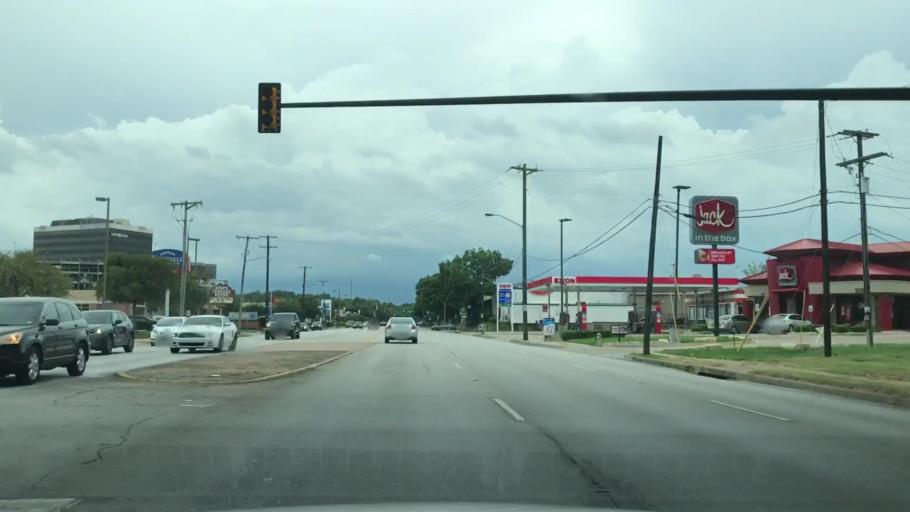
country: US
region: Texas
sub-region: Tarrant County
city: Fort Worth
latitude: 32.7309
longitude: -97.3615
